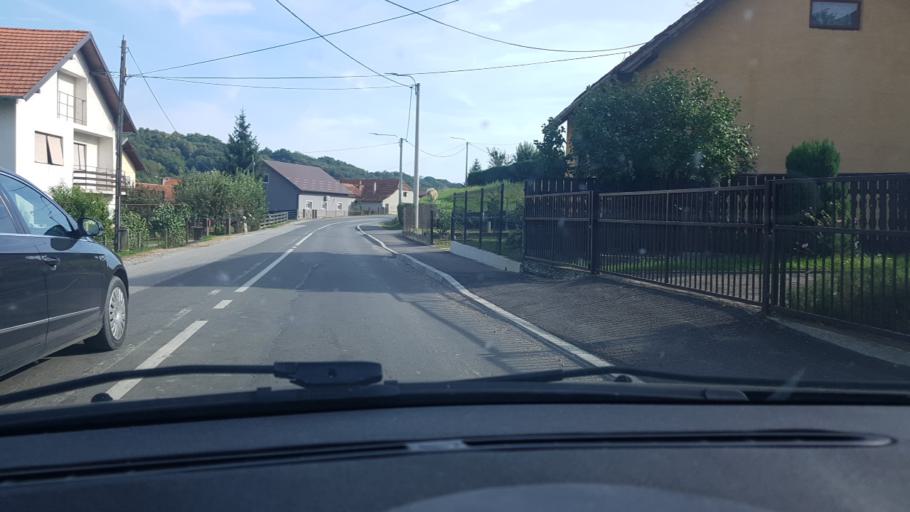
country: HR
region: Krapinsko-Zagorska
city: Zlatar
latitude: 46.0963
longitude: 16.0792
